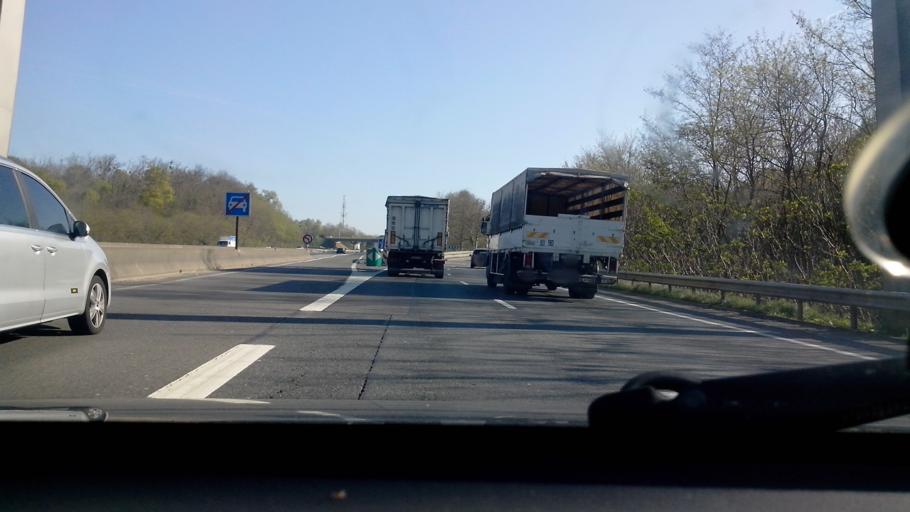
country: FR
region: Ile-de-France
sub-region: Departement de l'Essonne
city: Les Ulis
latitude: 48.6661
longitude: 2.1912
